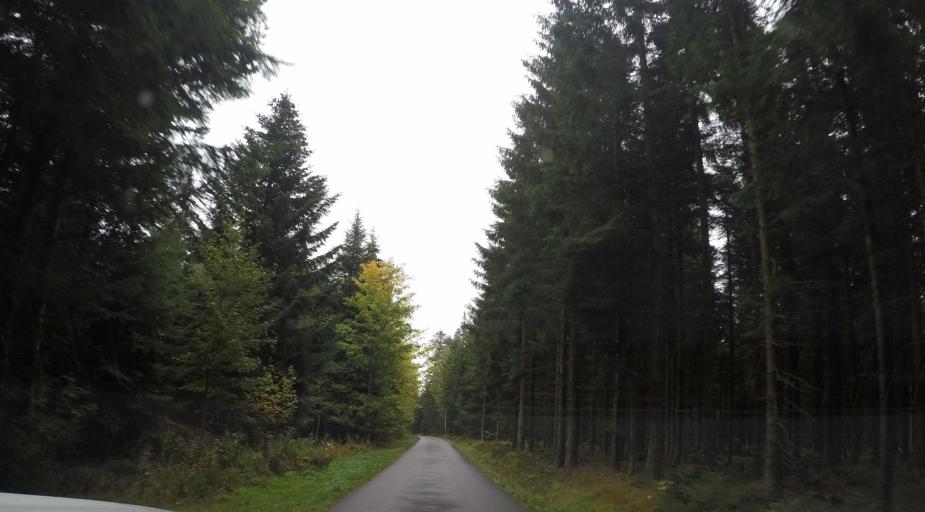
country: DE
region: Baden-Wuerttemberg
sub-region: Karlsruhe Region
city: Baiersbronn
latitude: 48.4787
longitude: 8.3036
